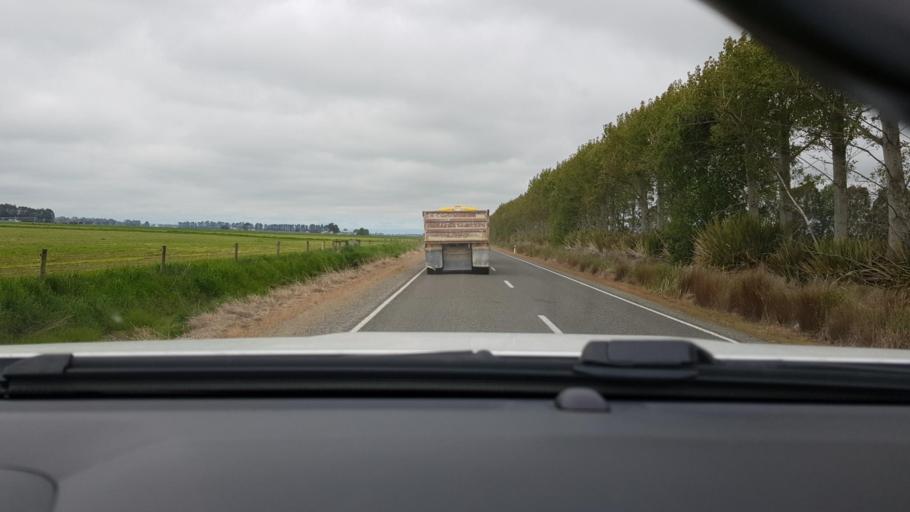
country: NZ
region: Otago
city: Oamaru
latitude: -44.9648
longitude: 170.9422
